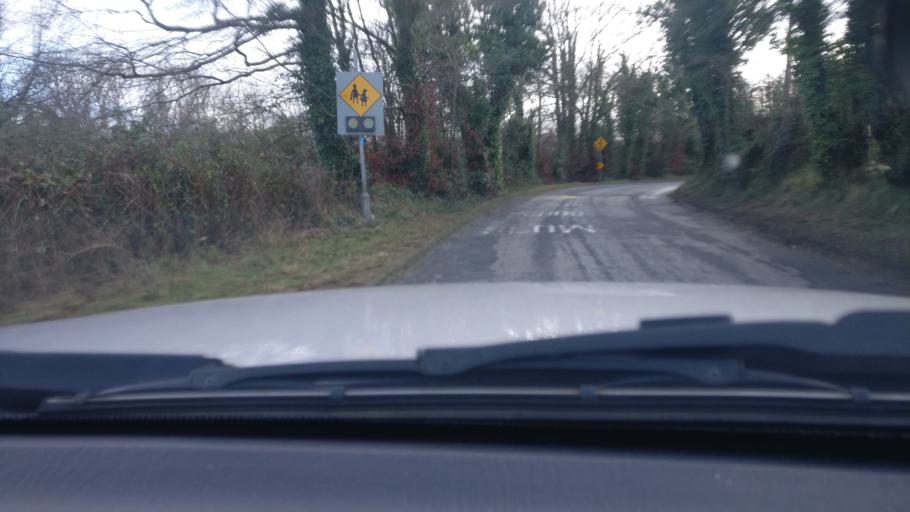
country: IE
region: Connaught
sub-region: County Galway
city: Ballinasloe
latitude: 53.2779
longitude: -8.2422
